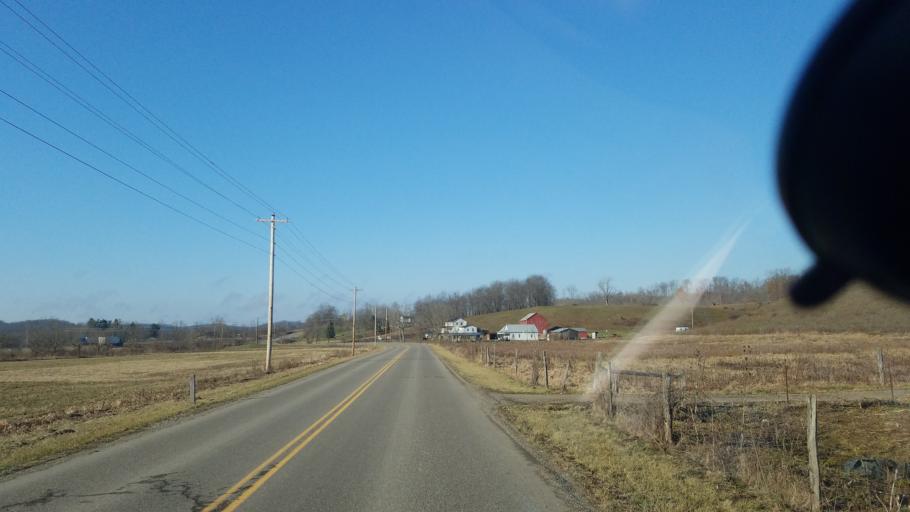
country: US
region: Ohio
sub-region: Belmont County
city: Barnesville
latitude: 40.0499
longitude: -81.3455
